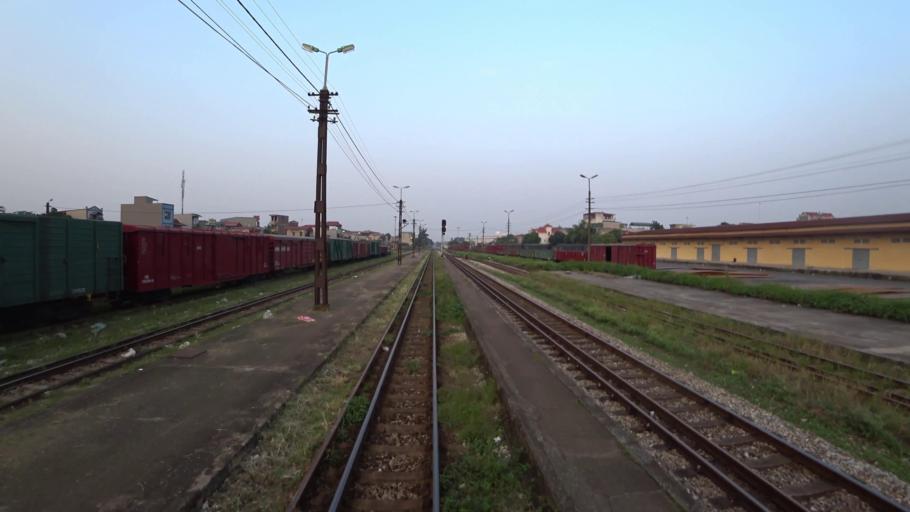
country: VN
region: Ha Noi
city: Dong Anh
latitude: 21.1028
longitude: 105.9041
